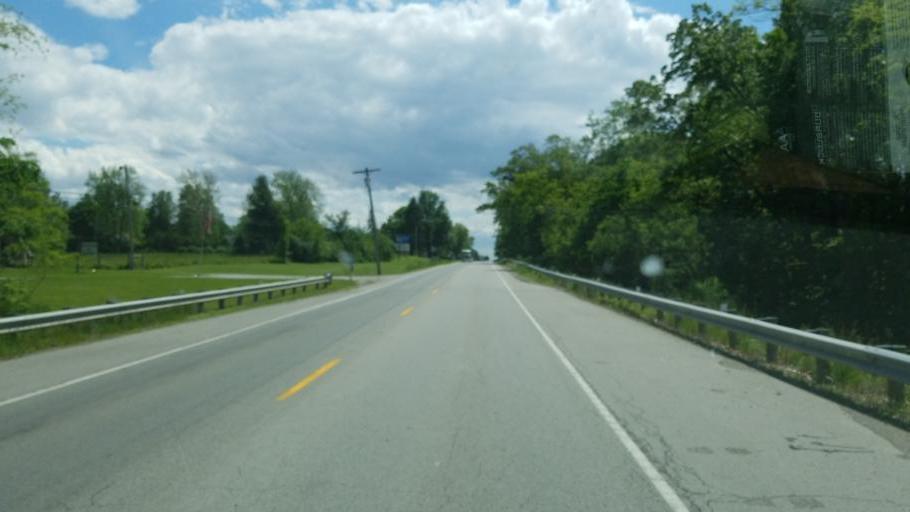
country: US
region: Ohio
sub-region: Erie County
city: Milan
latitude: 41.2851
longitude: -82.6060
